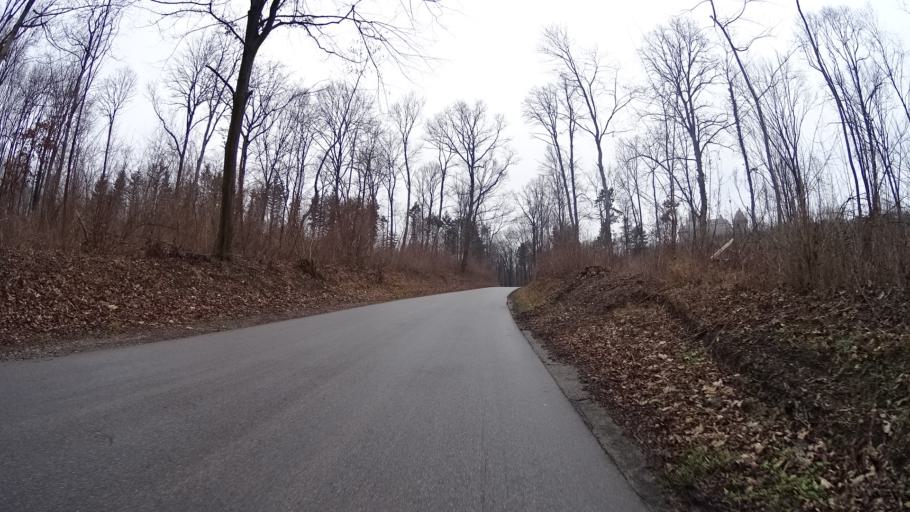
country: AT
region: Lower Austria
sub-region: Politischer Bezirk Korneuburg
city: Leobendorf
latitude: 48.3749
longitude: 16.3087
